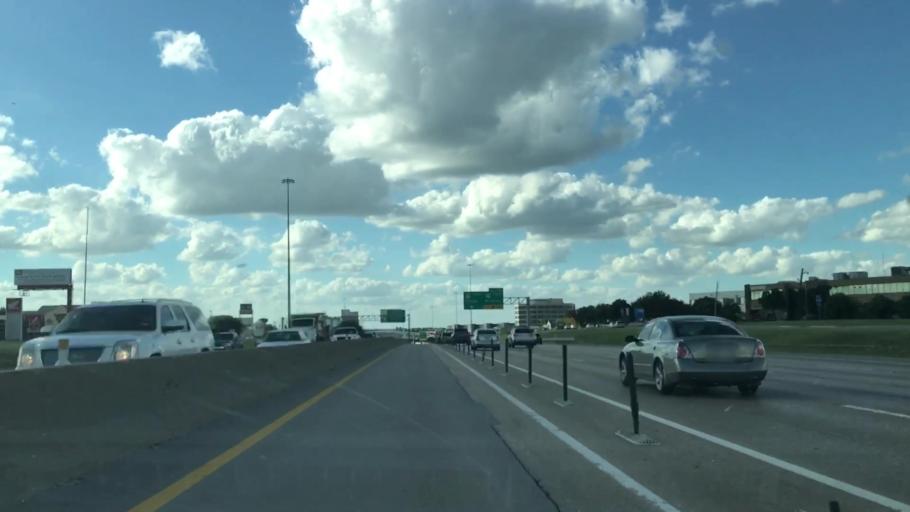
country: US
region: Texas
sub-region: Dallas County
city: Richardson
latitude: 32.9141
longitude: -96.7394
